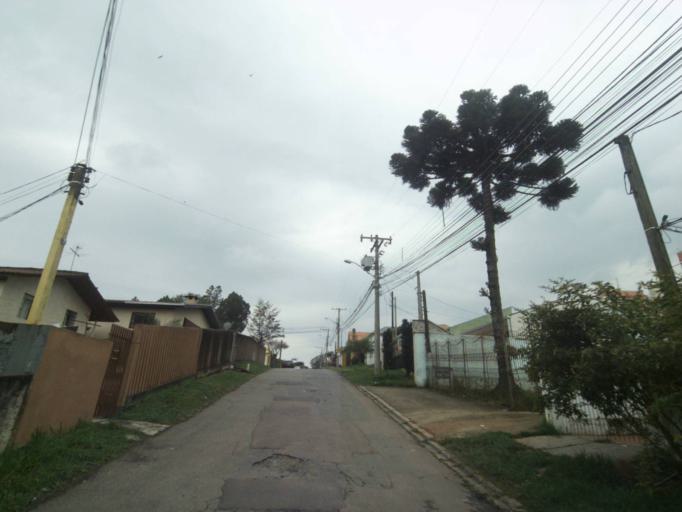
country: BR
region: Parana
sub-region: Curitiba
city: Curitiba
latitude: -25.4741
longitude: -49.3158
